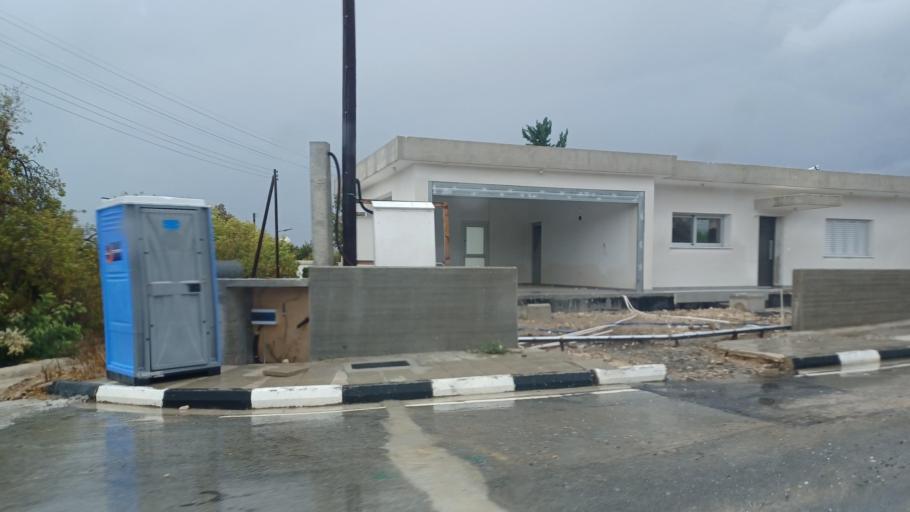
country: CY
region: Pafos
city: Mesogi
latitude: 34.7866
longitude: 32.4606
